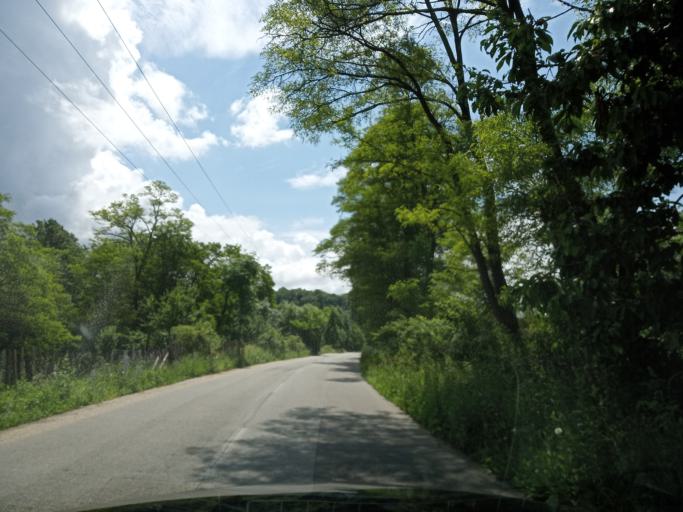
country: RO
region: Hunedoara
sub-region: Oras Petrila
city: Petrila
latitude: 45.4167
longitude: 23.4109
